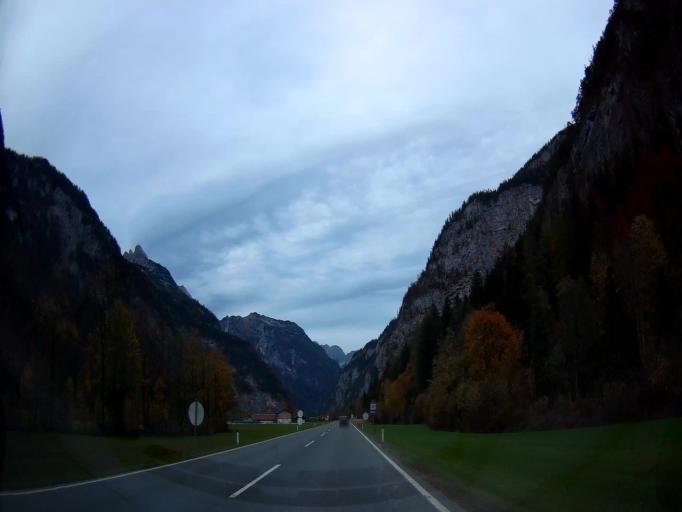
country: AT
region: Salzburg
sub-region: Politischer Bezirk Zell am See
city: Leogang
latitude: 47.4930
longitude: 12.8107
